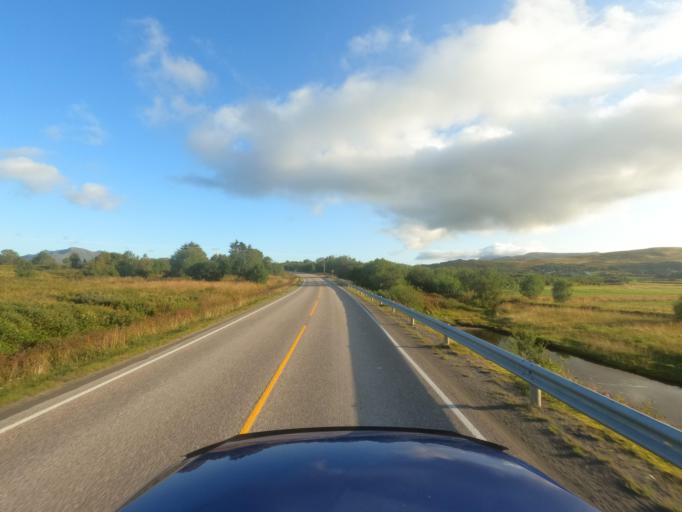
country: NO
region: Nordland
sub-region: Vestvagoy
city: Gravdal
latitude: 68.1446
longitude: 13.5467
